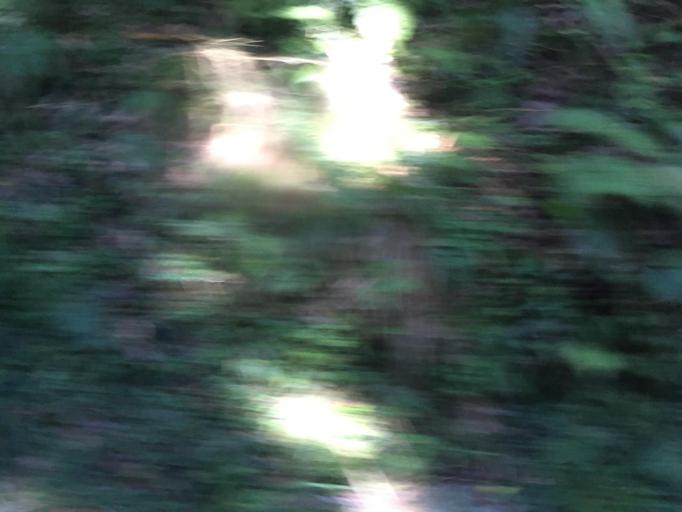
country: TW
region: Taiwan
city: Daxi
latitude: 24.6113
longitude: 121.4605
